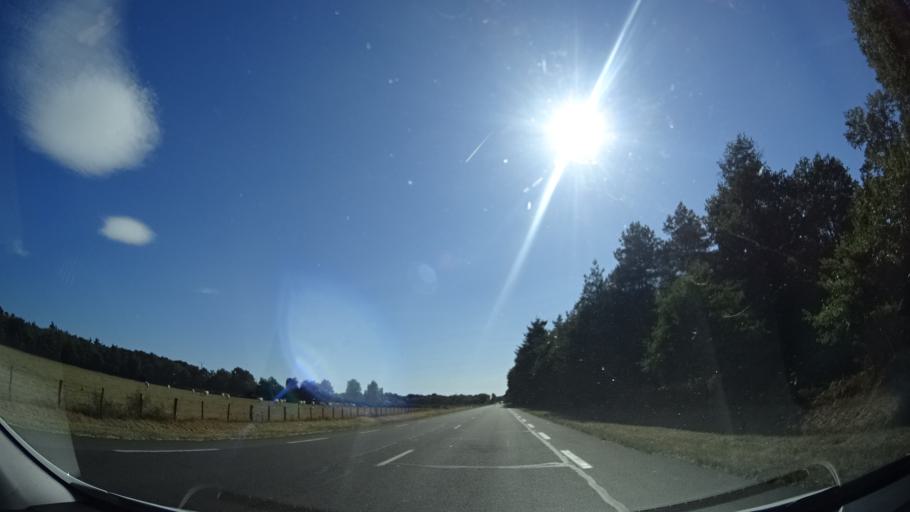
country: FR
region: Centre
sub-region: Departement du Loiret
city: Vitry-aux-Loges
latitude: 47.8976
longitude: 2.2795
